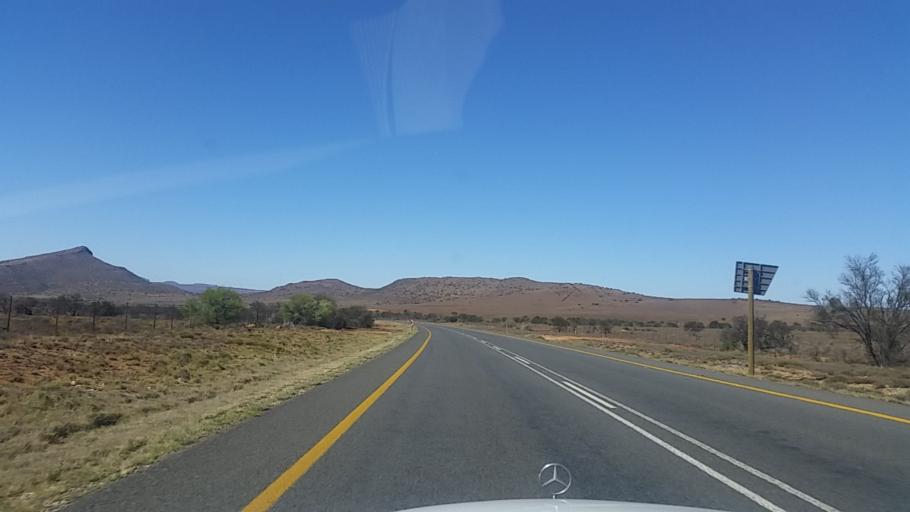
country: ZA
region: Eastern Cape
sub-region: Cacadu District Municipality
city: Graaff-Reinet
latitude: -32.0783
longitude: 24.6024
